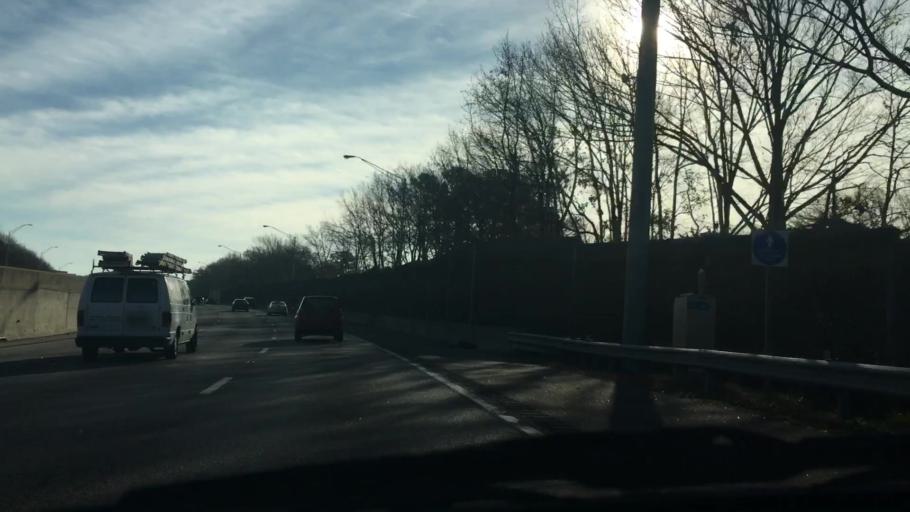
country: US
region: Virginia
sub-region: City of Norfolk
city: Norfolk
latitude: 36.8855
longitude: -76.2261
